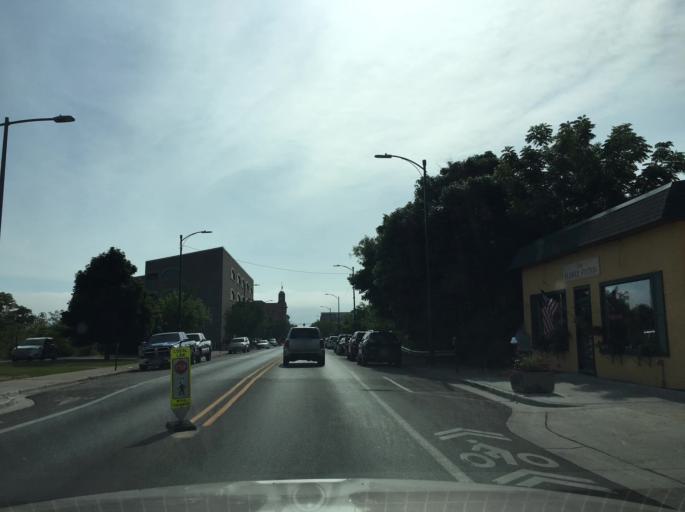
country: US
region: Michigan
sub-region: Grand Traverse County
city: Traverse City
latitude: 44.7640
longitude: -85.6283
